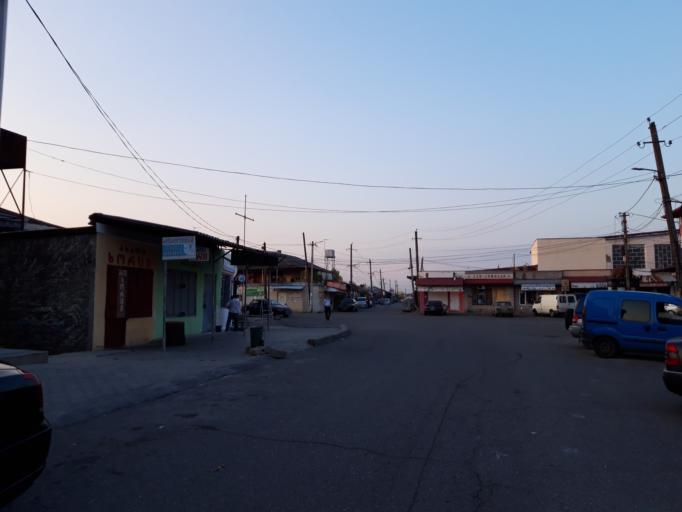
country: GE
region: Imereti
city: Samtredia
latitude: 42.1650
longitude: 42.3404
